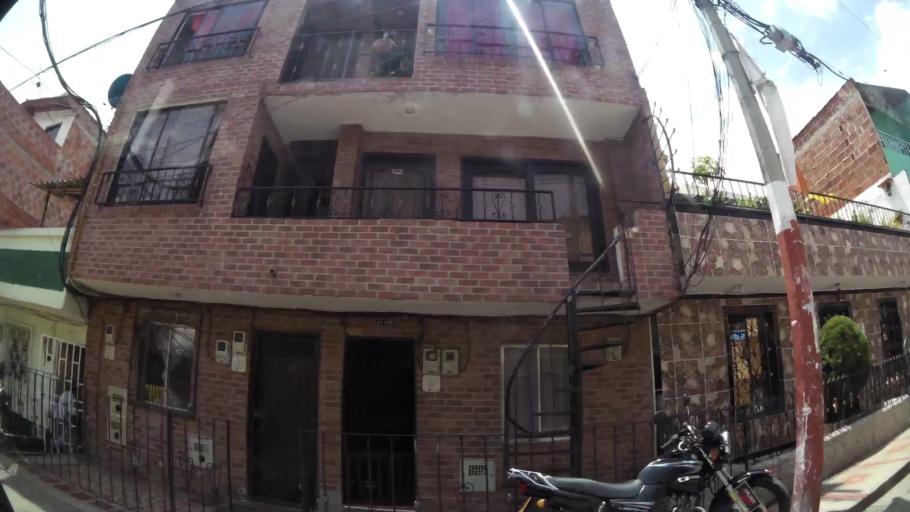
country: CO
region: Antioquia
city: Bello
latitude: 6.3472
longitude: -75.5638
